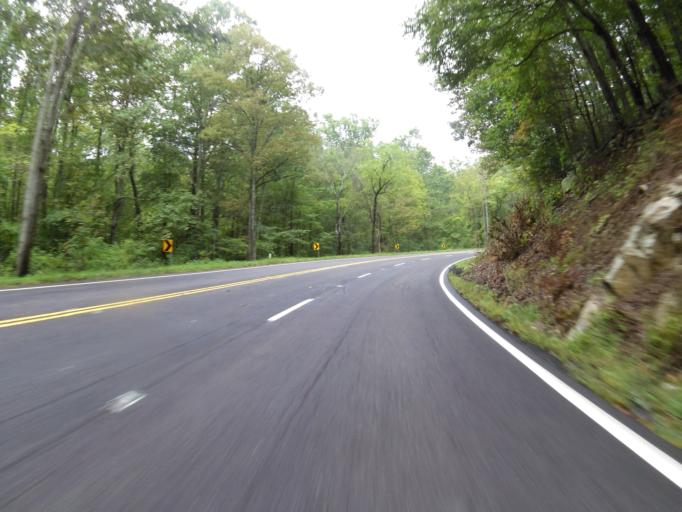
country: US
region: Virginia
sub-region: Rappahannock County
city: Washington
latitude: 38.6601
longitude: -78.2883
